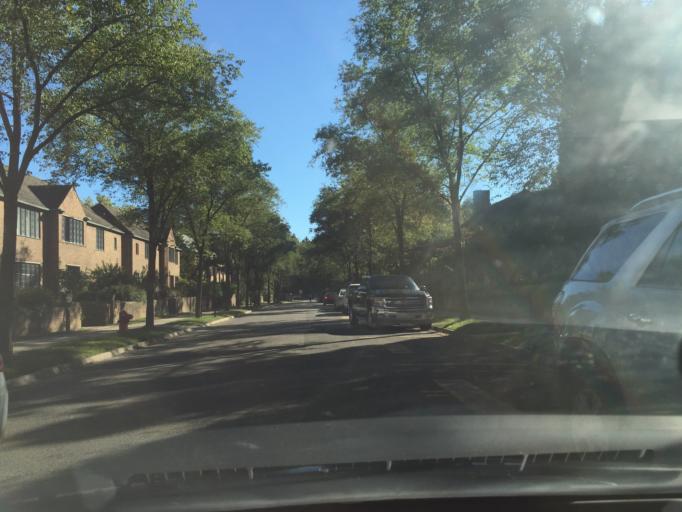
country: US
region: Michigan
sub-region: Oakland County
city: Bloomfield Hills
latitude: 42.5685
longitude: -83.2514
